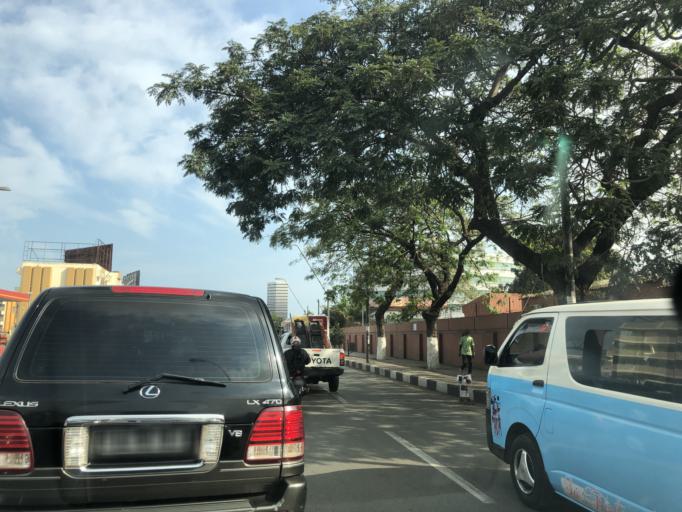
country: AO
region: Luanda
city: Luanda
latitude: -8.8419
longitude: 13.2325
